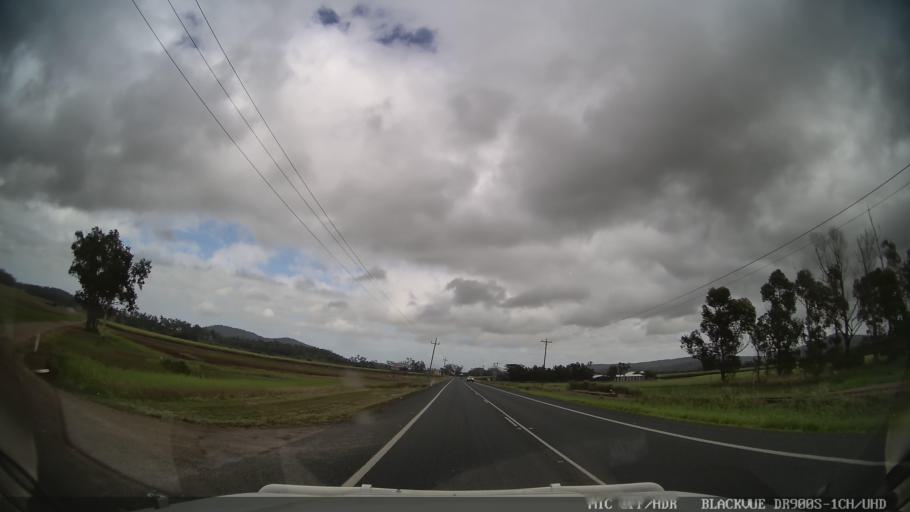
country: AU
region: Queensland
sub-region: Whitsunday
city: Proserpine
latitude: -20.3447
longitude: 148.6302
